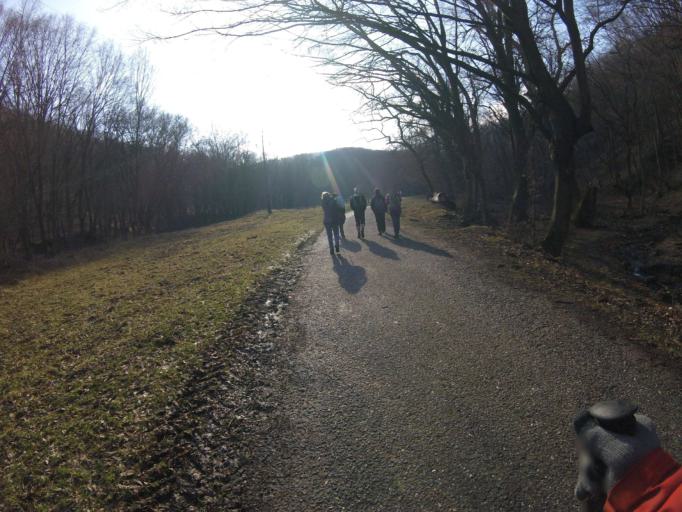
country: HU
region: Komarom-Esztergom
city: Pilismarot
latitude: 47.7486
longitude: 18.9028
